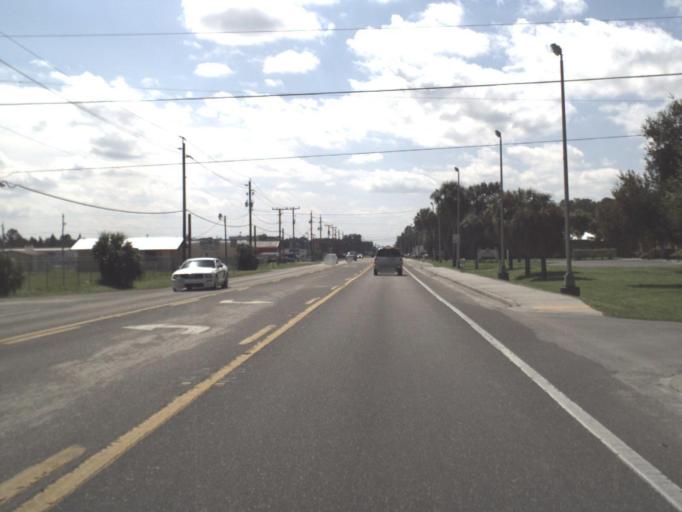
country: US
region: Florida
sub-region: Hendry County
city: LaBelle
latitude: 26.7534
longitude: -81.4382
